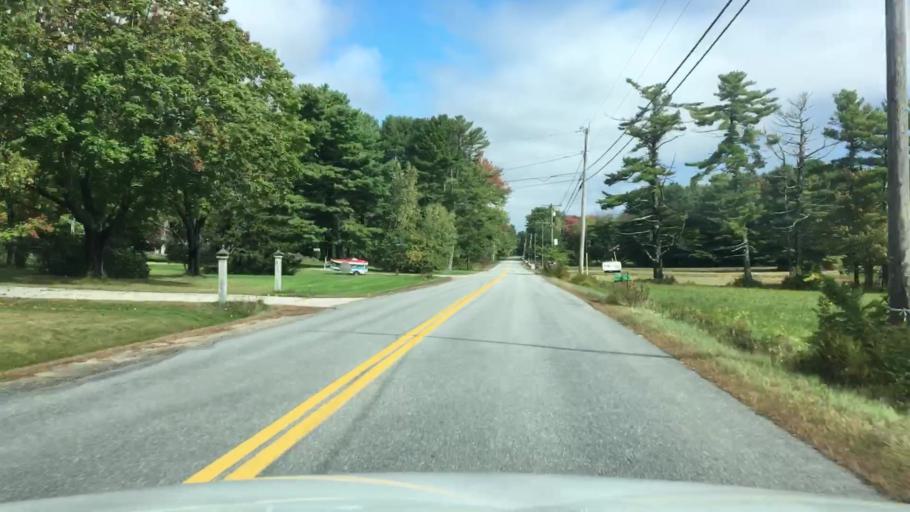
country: US
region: Maine
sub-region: Cumberland County
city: Brunswick
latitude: 43.9367
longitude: -69.9048
